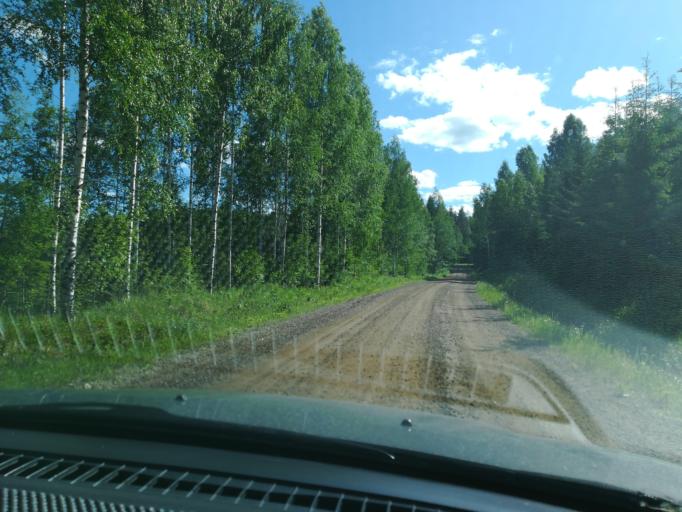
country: FI
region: Southern Savonia
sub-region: Mikkeli
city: Puumala
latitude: 61.6645
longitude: 28.1440
